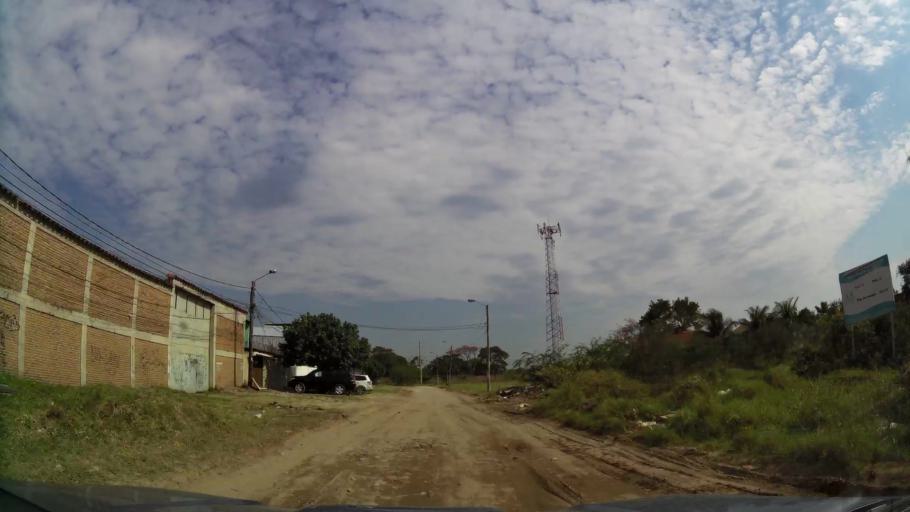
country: BO
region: Santa Cruz
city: Santa Cruz de la Sierra
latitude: -17.7264
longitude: -63.1734
